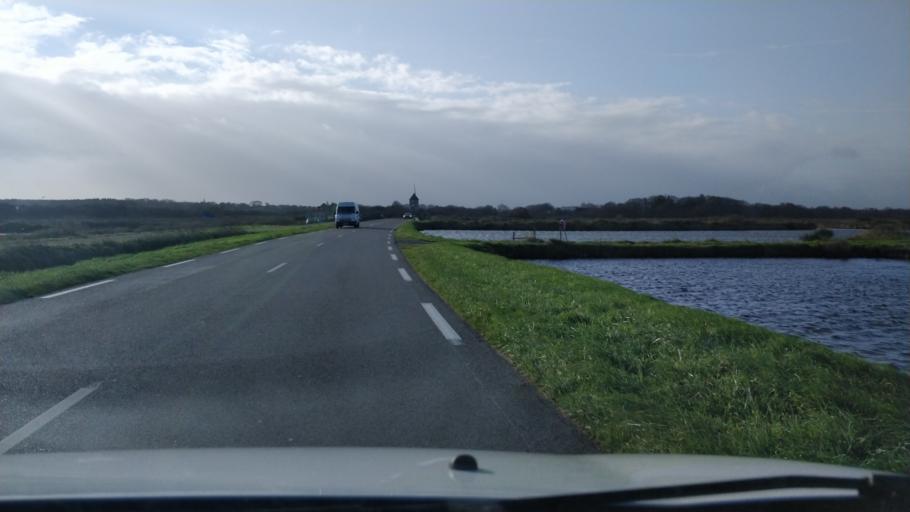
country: FR
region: Pays de la Loire
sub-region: Departement de la Loire-Atlantique
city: Asserac
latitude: 47.4090
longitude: -2.3986
